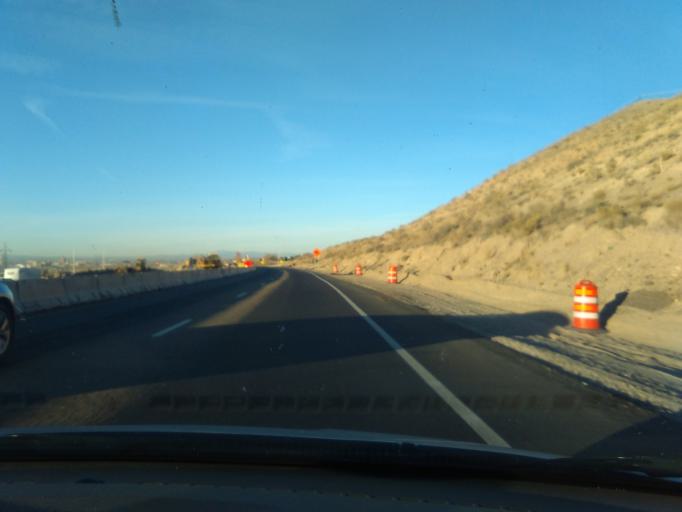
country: US
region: New Mexico
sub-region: Bernalillo County
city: South Valley
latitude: 35.0191
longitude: -106.6385
